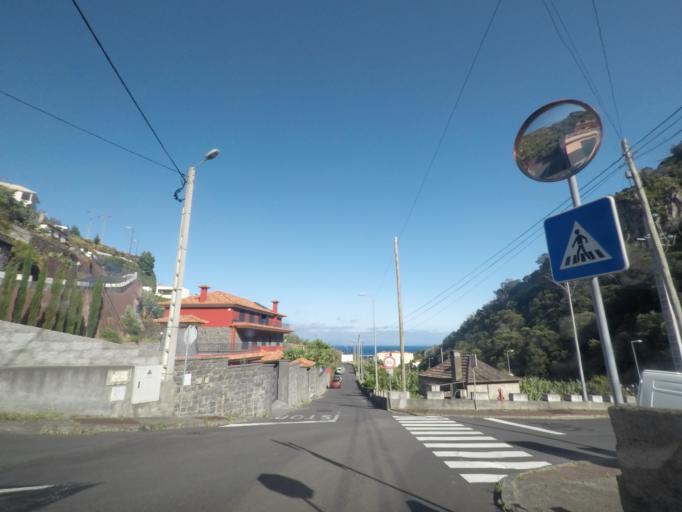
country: PT
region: Madeira
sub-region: Santa Cruz
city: Santa Cruz
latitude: 32.6927
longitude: -16.8011
